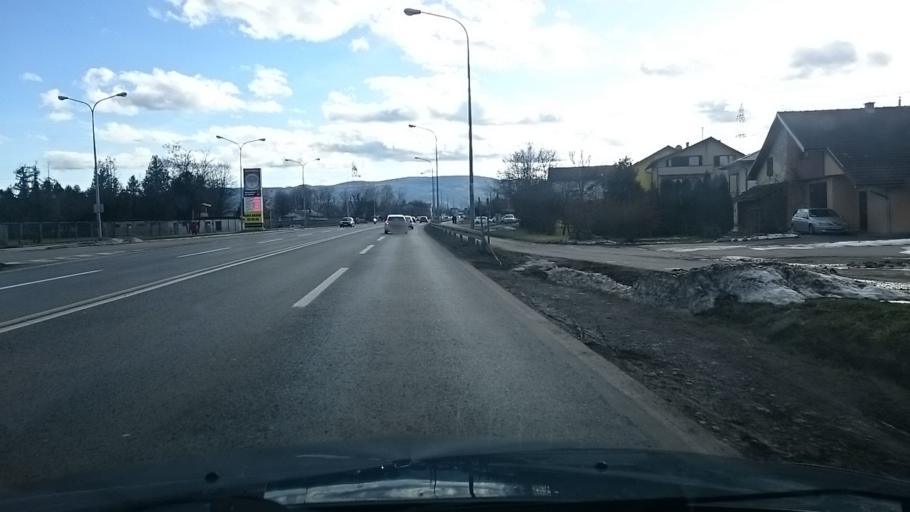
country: BA
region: Republika Srpska
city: Banja Luka
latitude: 44.8030
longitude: 17.1984
